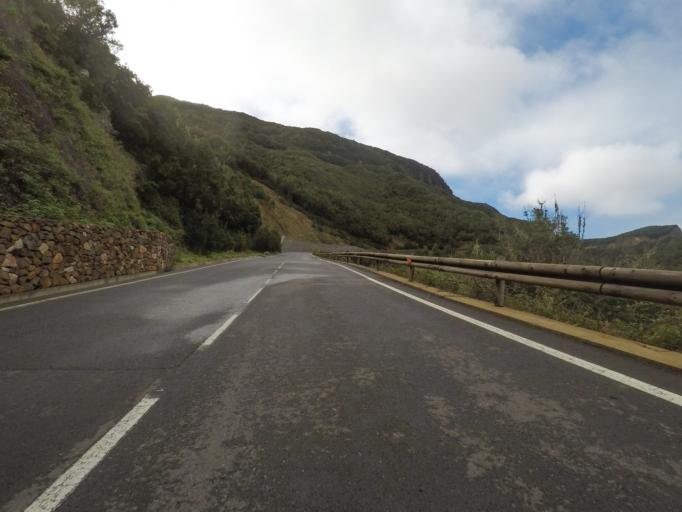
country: ES
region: Canary Islands
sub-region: Provincia de Santa Cruz de Tenerife
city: Vallehermosa
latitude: 28.1634
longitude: -17.2901
